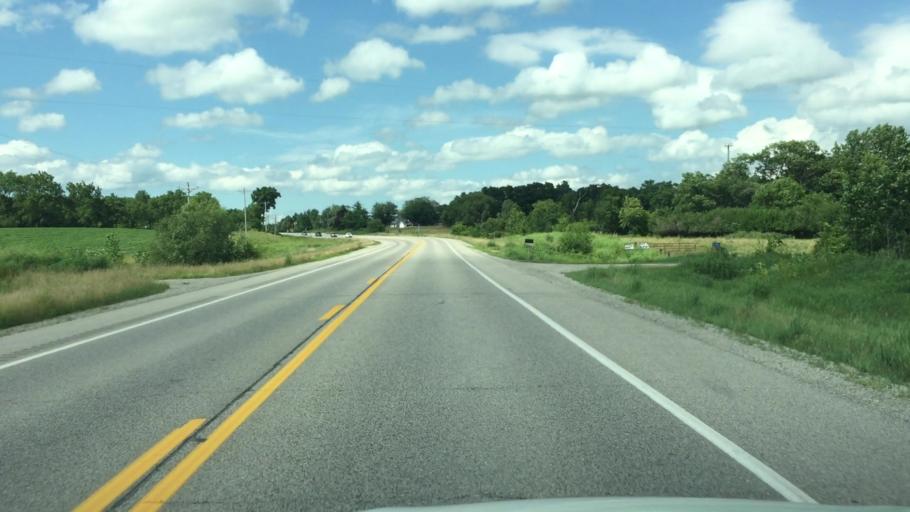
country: US
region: Iowa
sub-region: Johnson County
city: Solon
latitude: 41.7342
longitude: -91.4745
